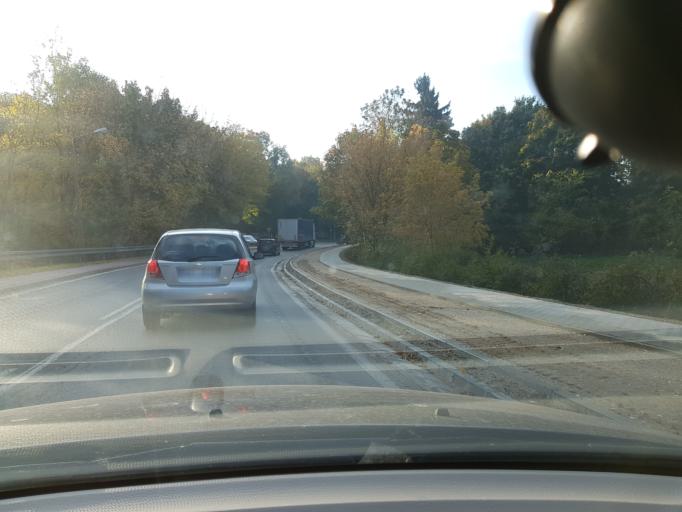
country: PL
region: Masovian Voivodeship
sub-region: Powiat otwocki
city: Jozefow
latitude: 52.1751
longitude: 21.2938
